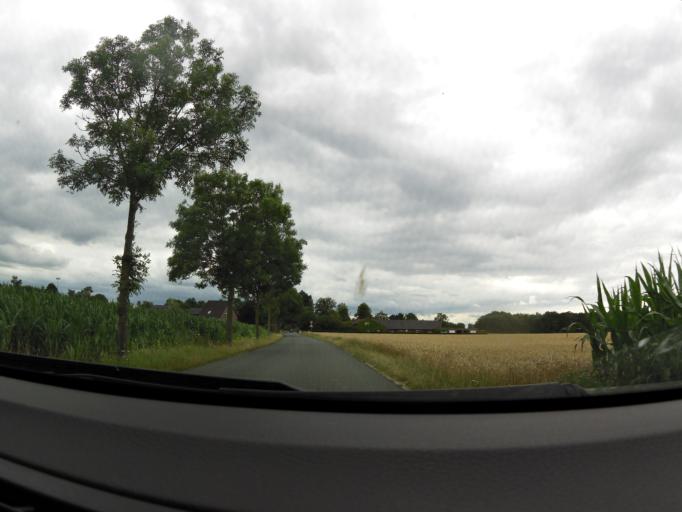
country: DE
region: North Rhine-Westphalia
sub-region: Regierungsbezirk Dusseldorf
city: Sonsbeck
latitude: 51.5883
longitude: 6.3478
